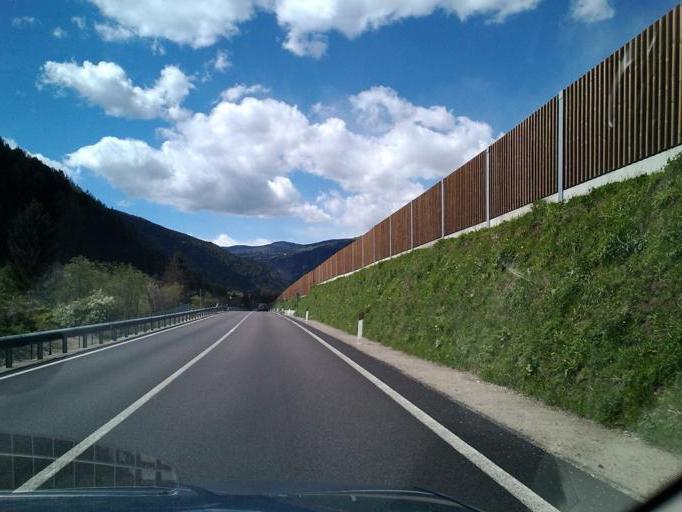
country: IT
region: Trentino-Alto Adige
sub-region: Bolzano
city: Terento
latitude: 46.8102
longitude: 11.7562
